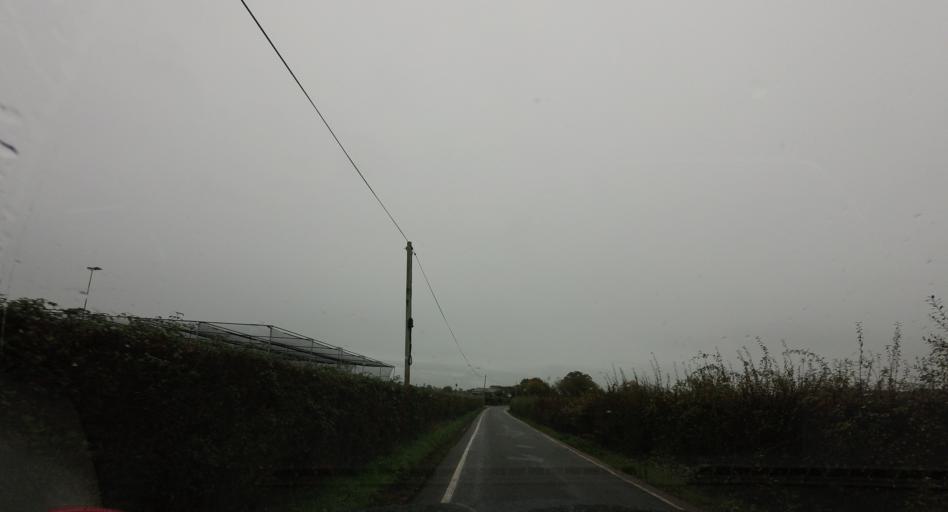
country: GB
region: England
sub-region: Kent
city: Tonbridge
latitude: 51.1884
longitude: 0.2498
